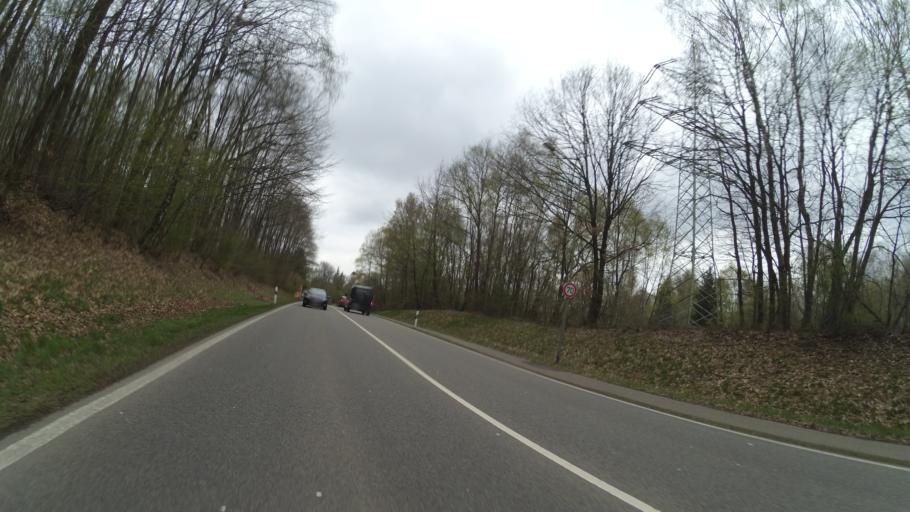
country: DE
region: Saarland
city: Friedrichsthal
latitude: 49.3400
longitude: 7.0764
